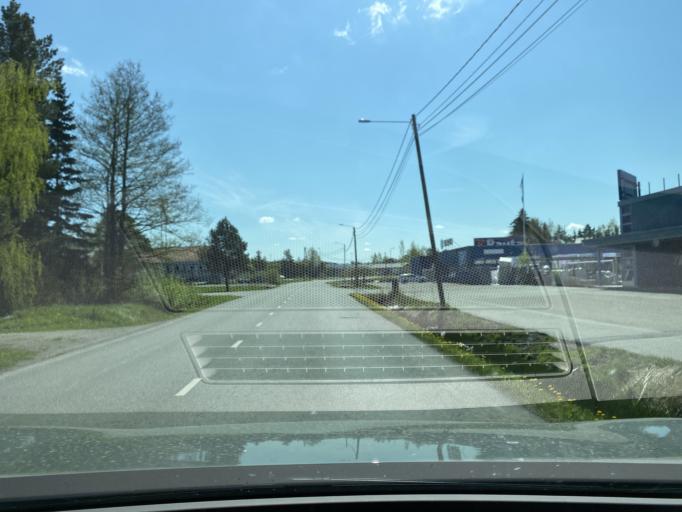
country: FI
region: Pirkanmaa
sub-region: Lounais-Pirkanmaa
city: Vammala
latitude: 61.3276
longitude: 22.9138
